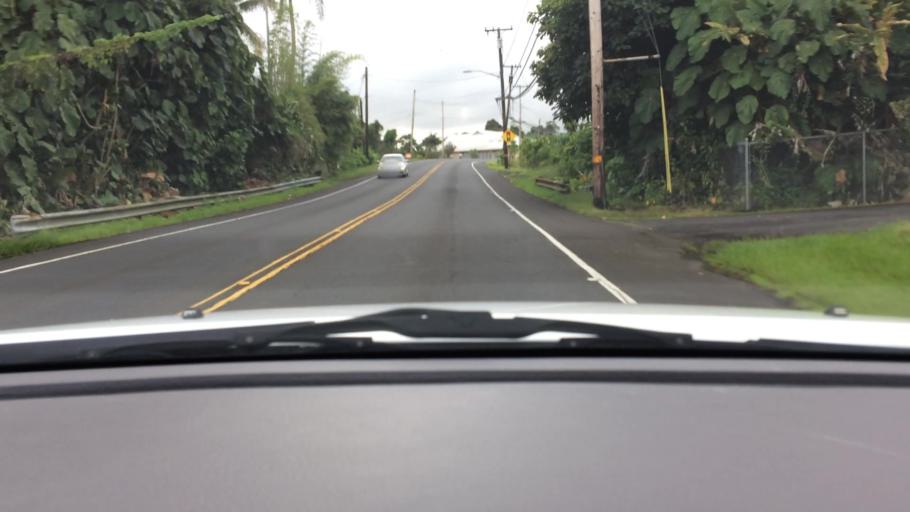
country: US
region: Hawaii
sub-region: Hawaii County
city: Hilo
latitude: 19.6968
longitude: -155.0707
